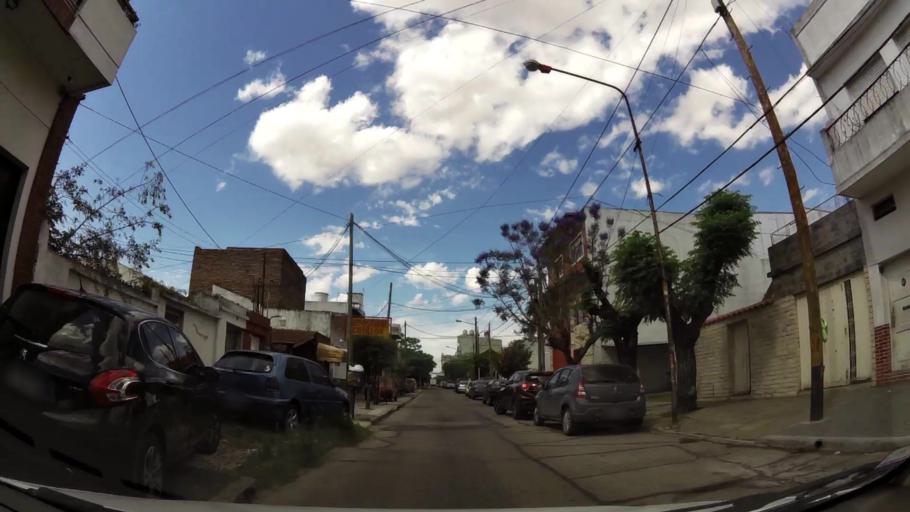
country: AR
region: Buenos Aires
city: San Justo
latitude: -34.6503
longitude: -58.5496
